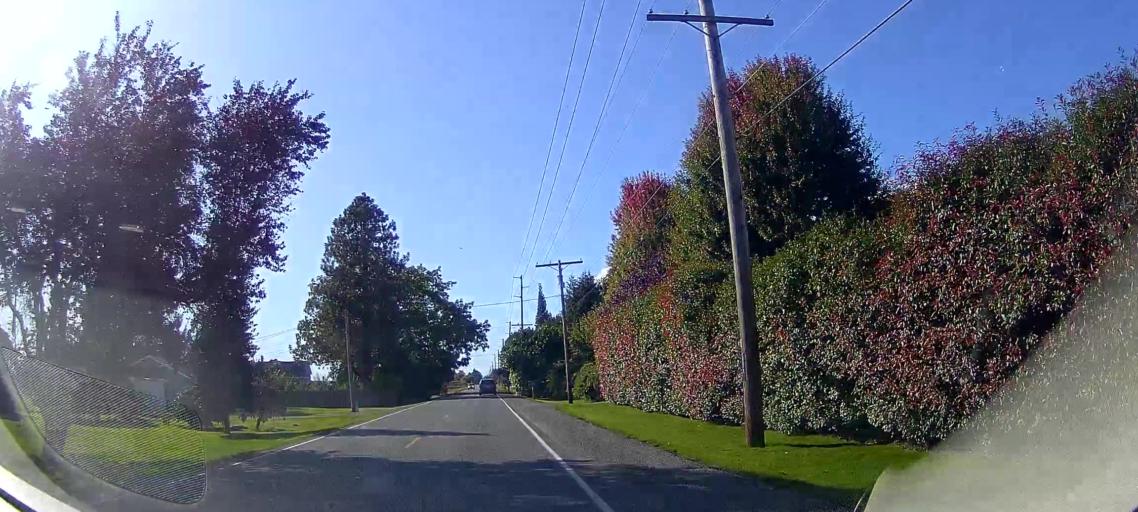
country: US
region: Washington
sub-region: Skagit County
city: Mount Vernon
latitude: 48.4426
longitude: -122.3833
